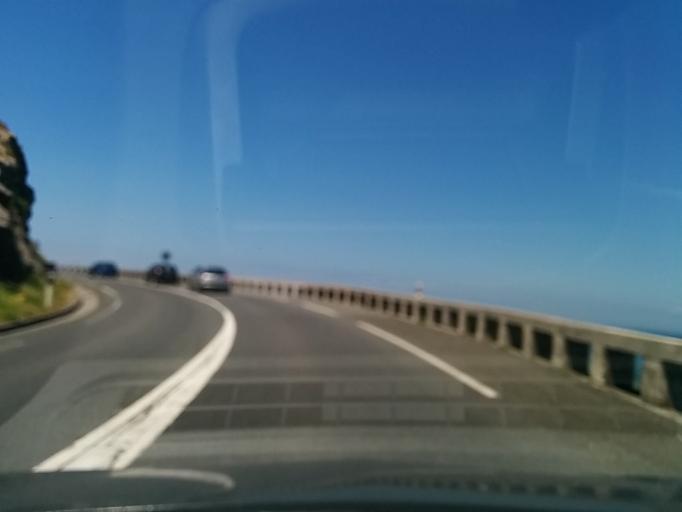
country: ES
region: Basque Country
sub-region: Provincia de Guipuzcoa
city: Getaria
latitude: 43.3053
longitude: -2.2085
